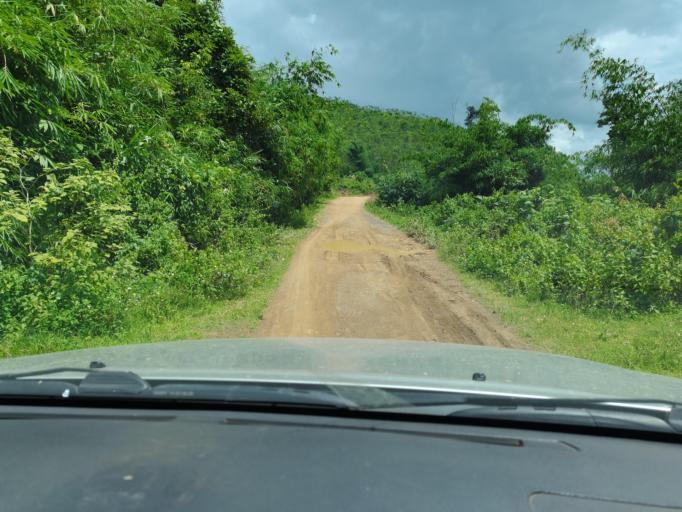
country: LA
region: Loungnamtha
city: Muang Long
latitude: 20.7226
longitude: 101.0140
